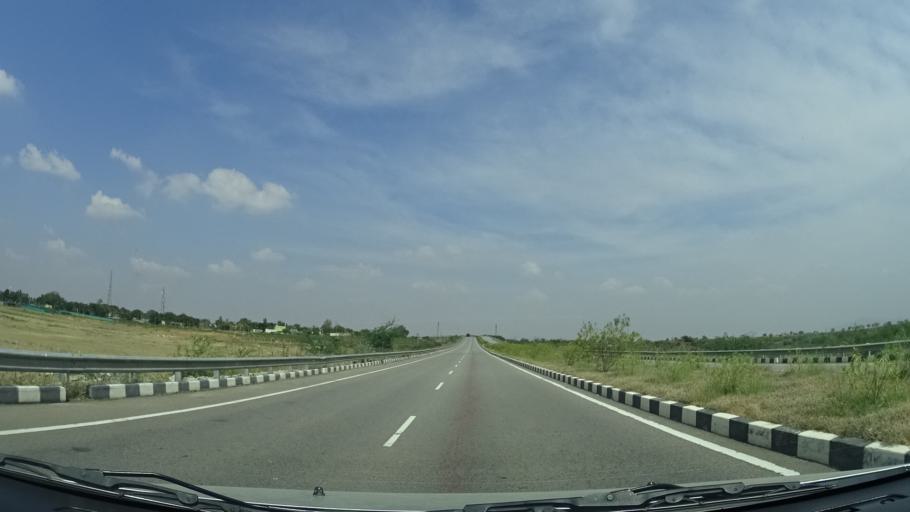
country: IN
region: Andhra Pradesh
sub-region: Anantapur
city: Dharmavaram
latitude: 14.3085
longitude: 77.6335
